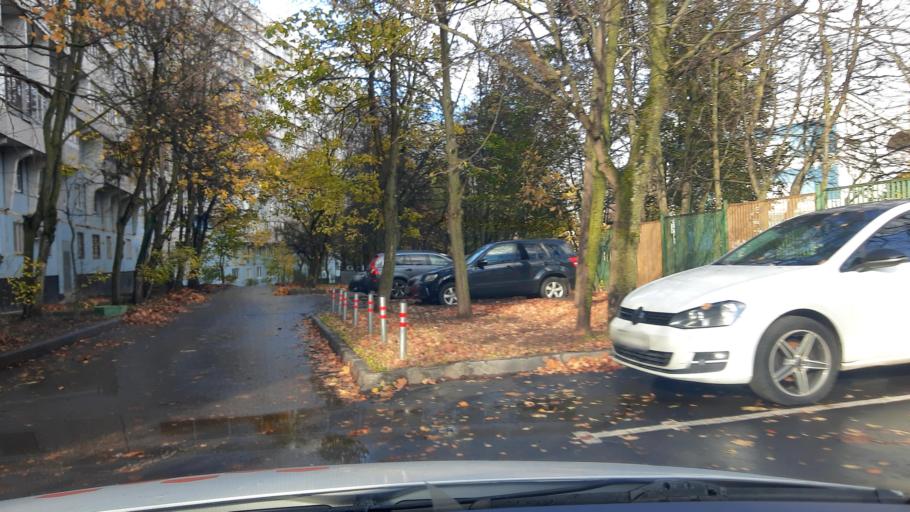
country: RU
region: Moscow
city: Chertanovo Yuzhnoye
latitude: 55.5980
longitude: 37.5814
